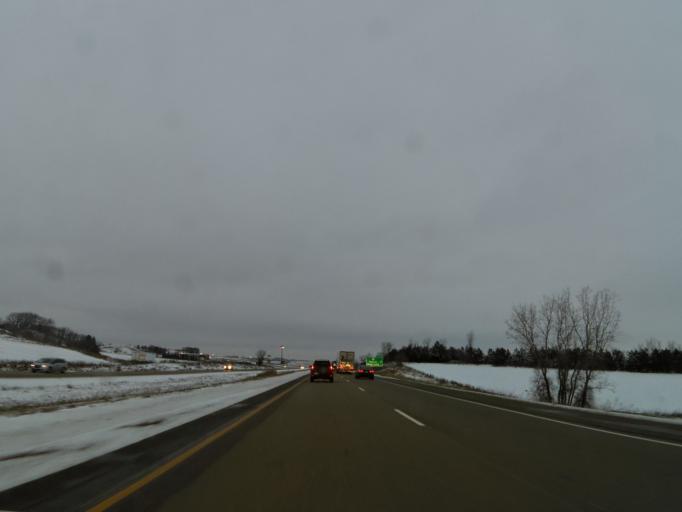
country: US
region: Wisconsin
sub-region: Saint Croix County
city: Roberts
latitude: 44.9544
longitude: -92.5497
